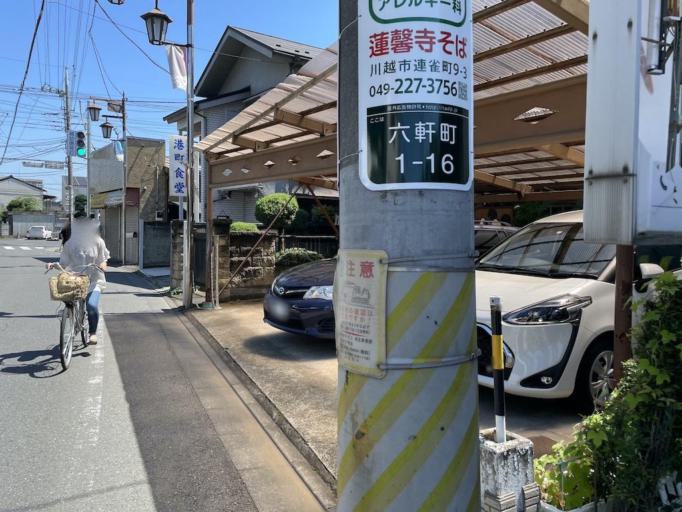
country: JP
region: Saitama
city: Kawagoe
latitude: 35.9179
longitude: 139.4790
